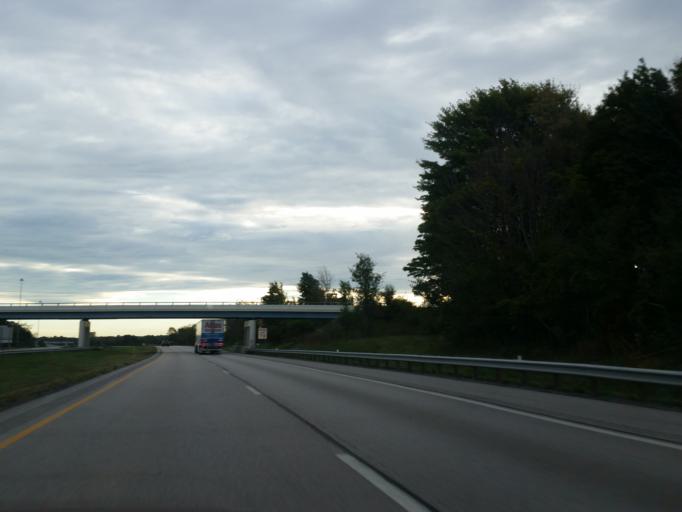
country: US
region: Ohio
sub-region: Ashtabula County
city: Conneaut
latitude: 41.9200
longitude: -80.5565
